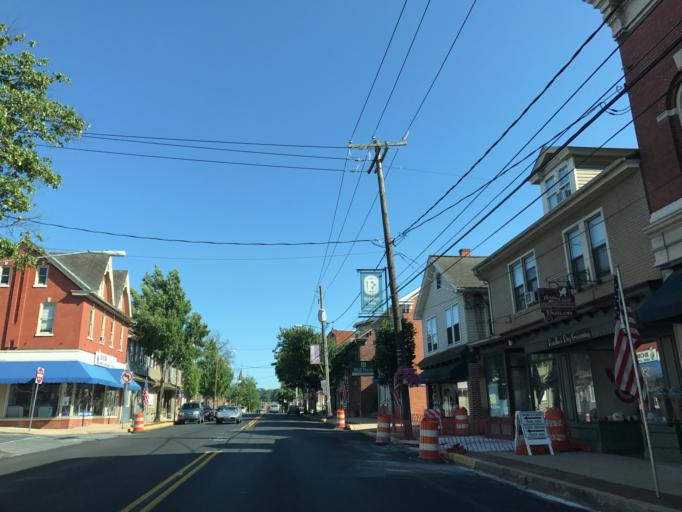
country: US
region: Pennsylvania
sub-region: Lancaster County
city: Elizabethtown
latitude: 40.1505
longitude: -76.6053
